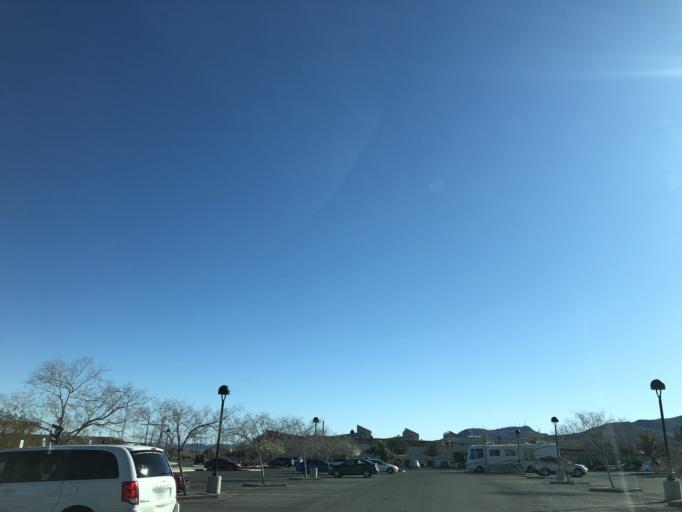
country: US
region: Nevada
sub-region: Clark County
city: Whitney
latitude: 36.0177
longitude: -115.0817
